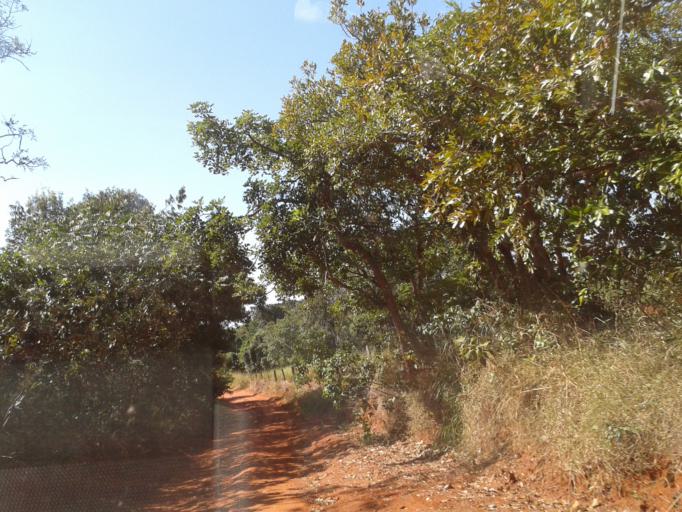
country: BR
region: Minas Gerais
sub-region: Campina Verde
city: Campina Verde
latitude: -19.4404
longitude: -49.5752
